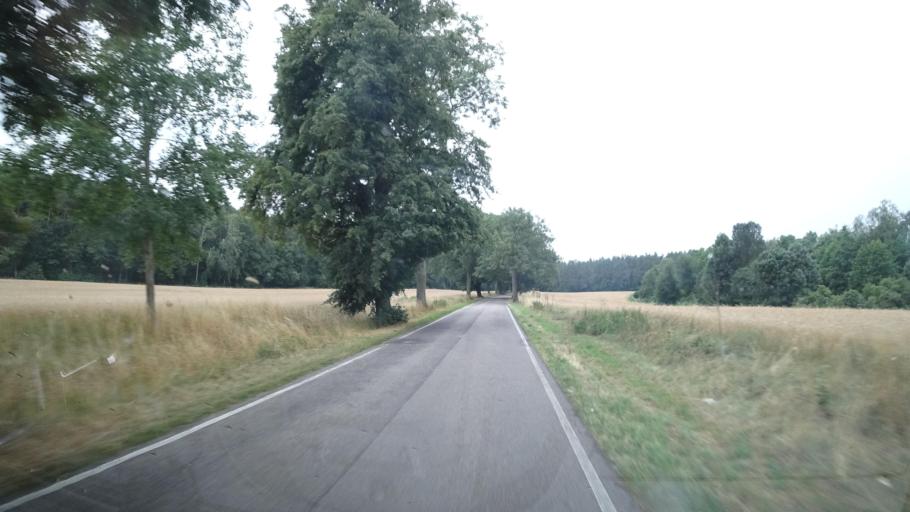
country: PL
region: Warmian-Masurian Voivodeship
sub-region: Powiat gizycki
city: Ryn
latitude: 53.8957
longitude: 21.5731
